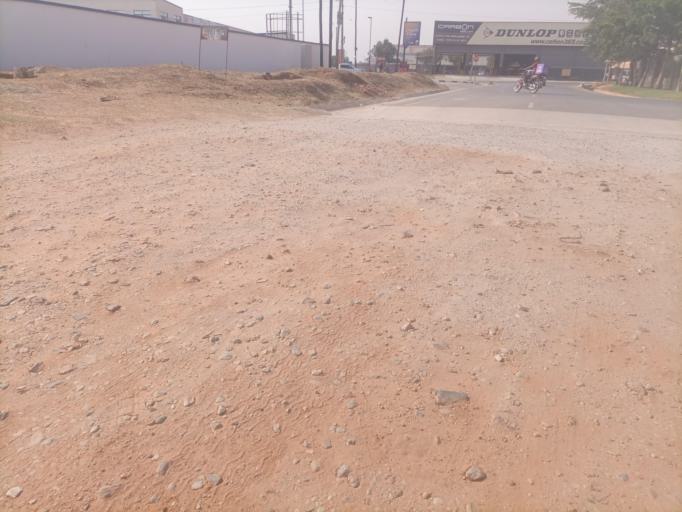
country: ZM
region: Lusaka
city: Lusaka
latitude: -15.3990
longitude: 28.3939
